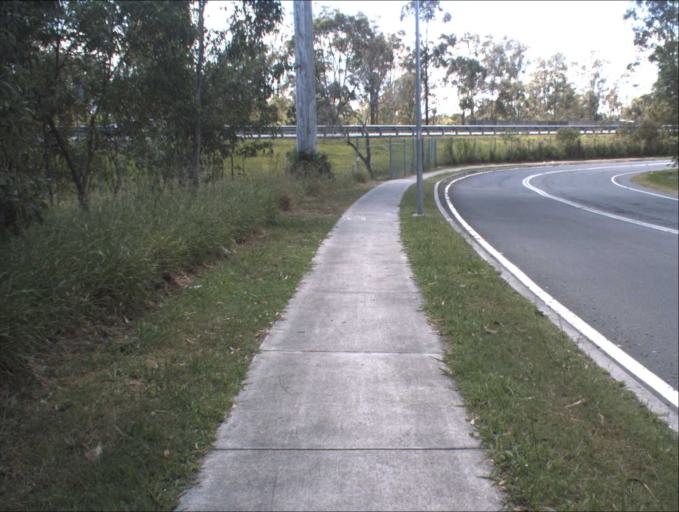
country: AU
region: Queensland
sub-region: Logan
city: Woodridge
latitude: -27.6593
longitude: 153.0881
